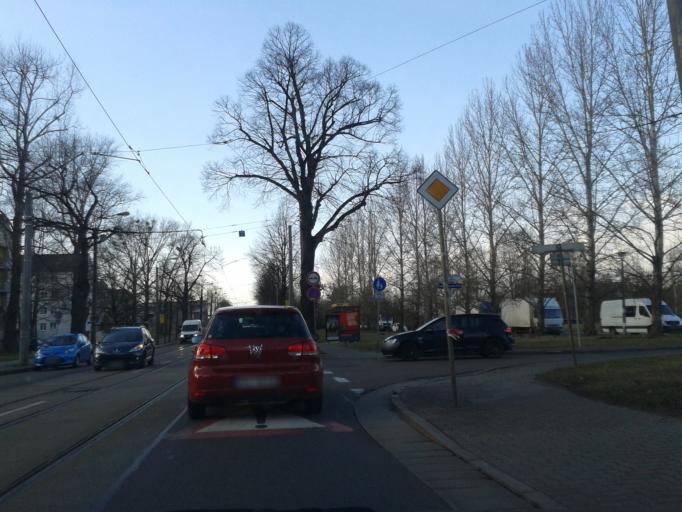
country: DE
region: Saxony
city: Dresden
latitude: 51.0172
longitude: 13.7847
